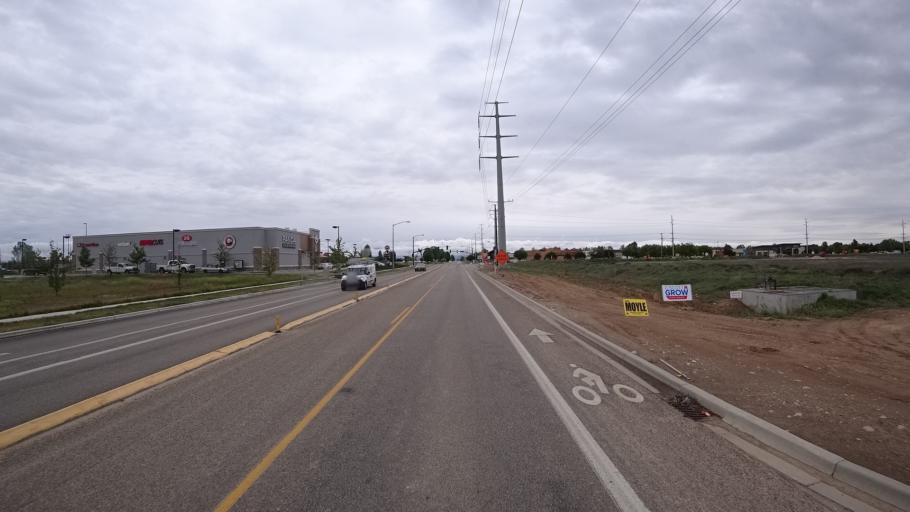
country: US
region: Idaho
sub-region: Ada County
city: Meridian
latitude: 43.6485
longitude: -116.4354
